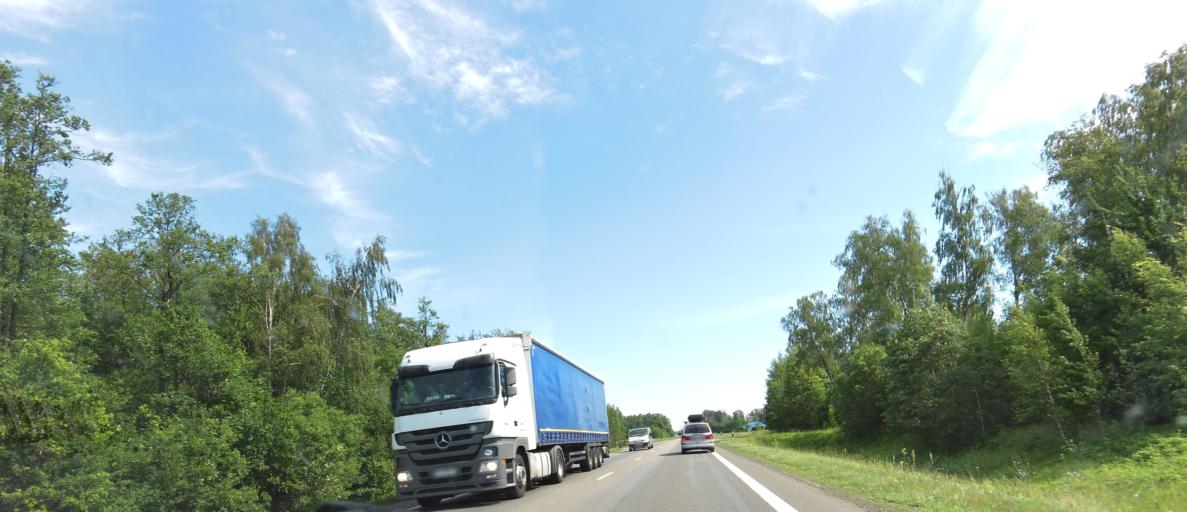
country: LT
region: Panevezys
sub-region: Panevezys City
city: Panevezys
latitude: 55.7630
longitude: 24.2885
